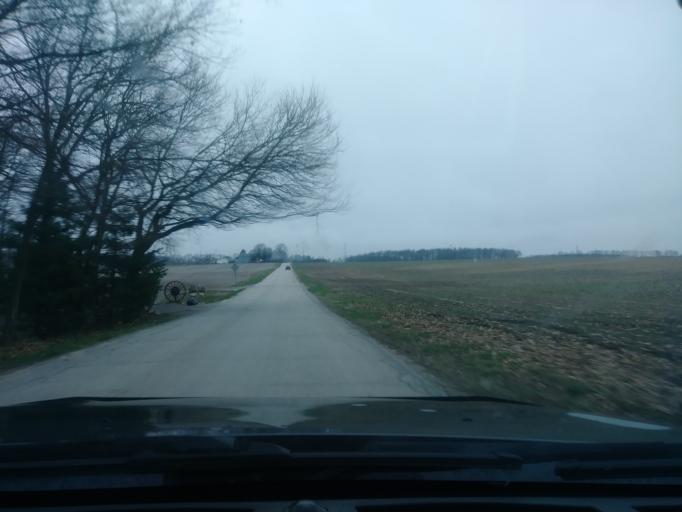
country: US
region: Indiana
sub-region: LaPorte County
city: Westville
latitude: 41.5334
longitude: -86.7990
